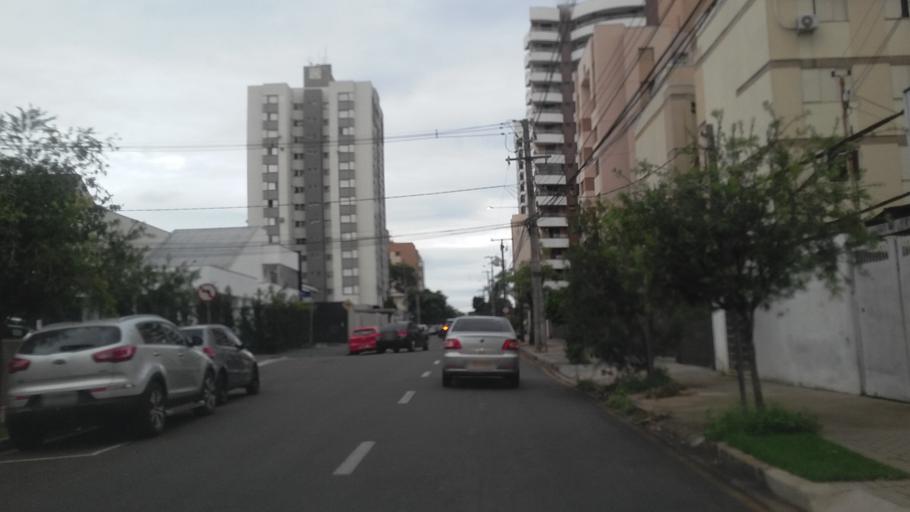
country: BR
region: Parana
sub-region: Londrina
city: Londrina
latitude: -23.3085
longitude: -51.1793
